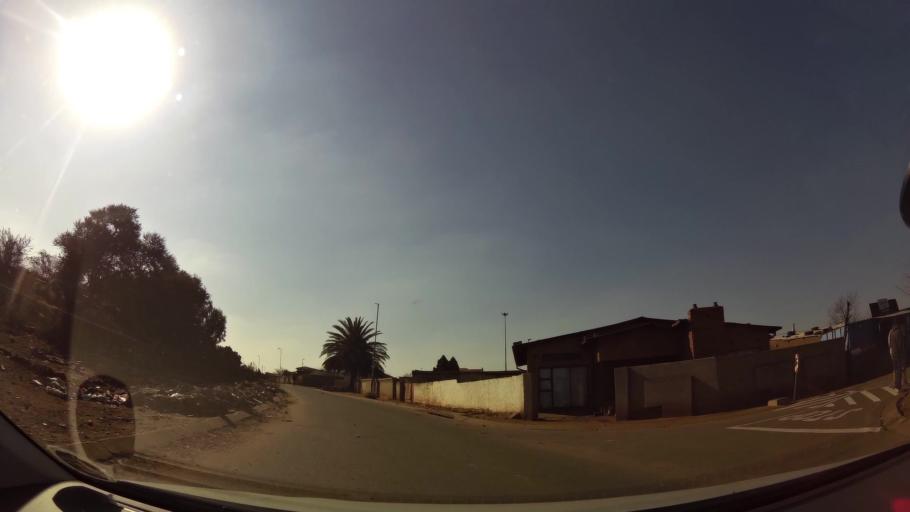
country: ZA
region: Gauteng
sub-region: City of Johannesburg Metropolitan Municipality
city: Soweto
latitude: -26.2850
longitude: 27.8664
